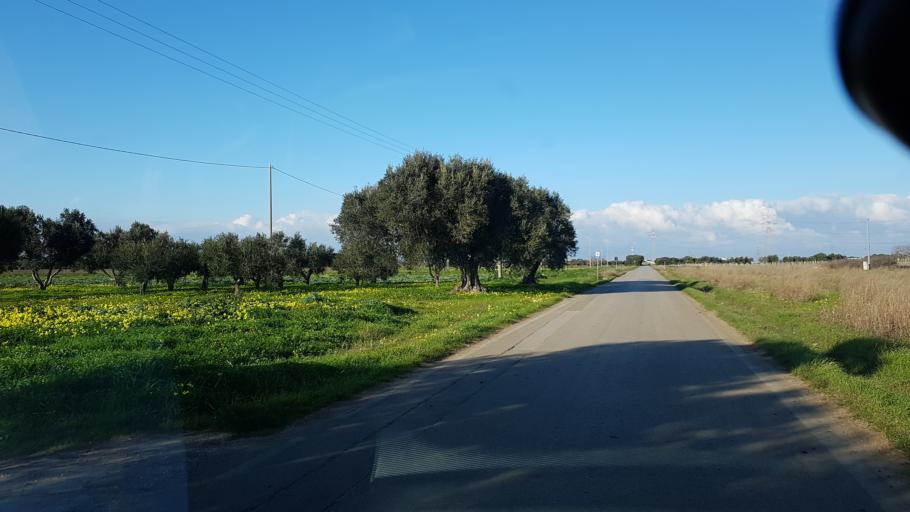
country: IT
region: Apulia
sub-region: Provincia di Brindisi
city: La Rosa
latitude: 40.5799
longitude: 17.9020
